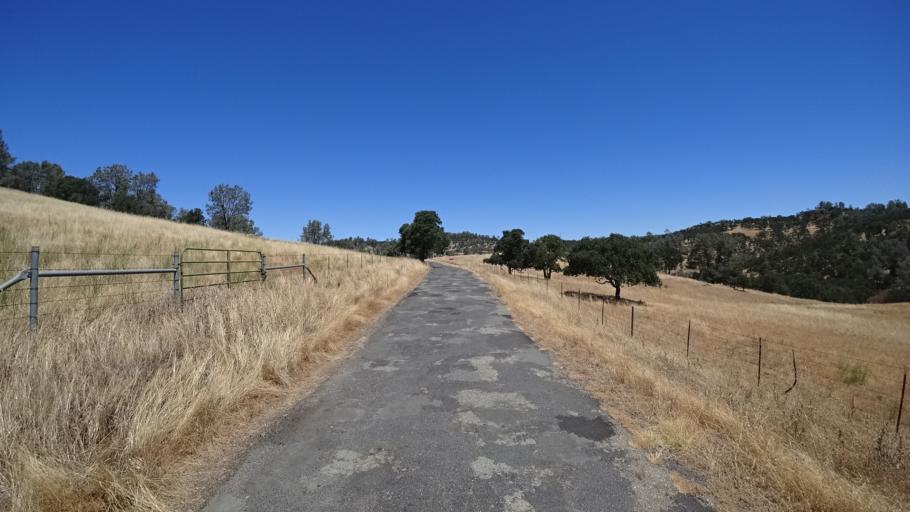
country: US
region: California
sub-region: Calaveras County
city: Rancho Calaveras
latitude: 38.0530
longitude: -120.8022
